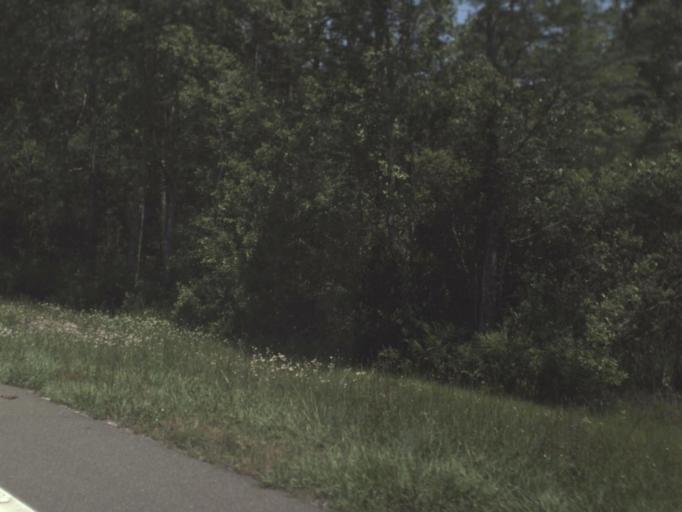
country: US
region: Florida
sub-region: Baker County
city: Macclenny
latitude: 30.2647
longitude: -82.2237
